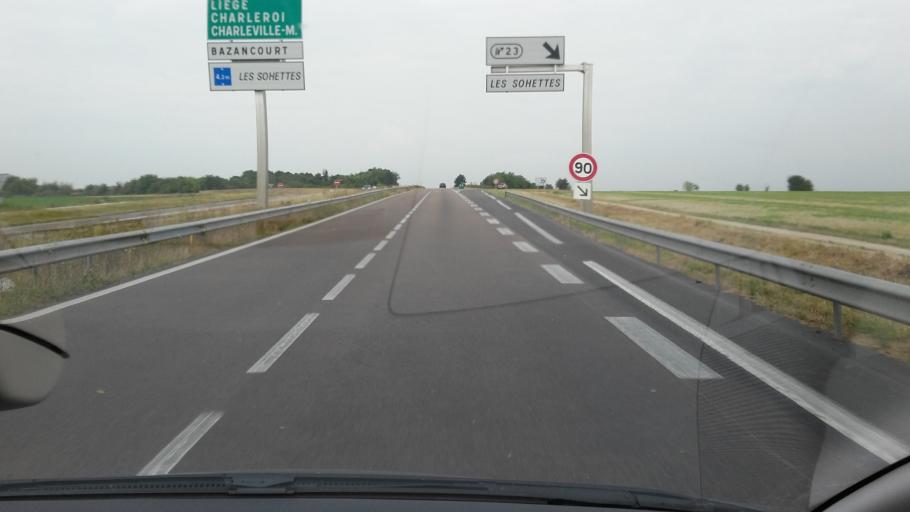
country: FR
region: Champagne-Ardenne
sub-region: Departement de la Marne
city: Bazancourt
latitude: 49.3366
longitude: 4.1772
